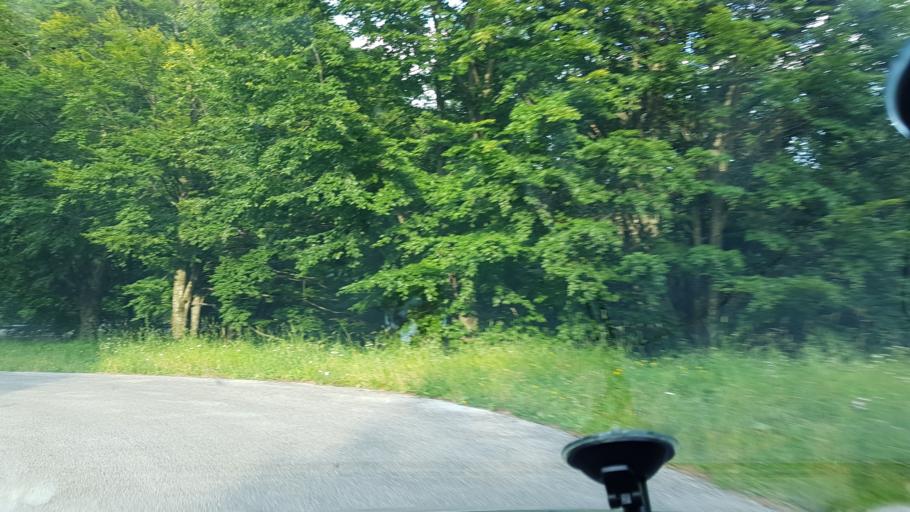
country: IT
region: Friuli Venezia Giulia
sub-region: Provincia di Udine
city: Prato
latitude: 46.3317
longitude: 13.3400
